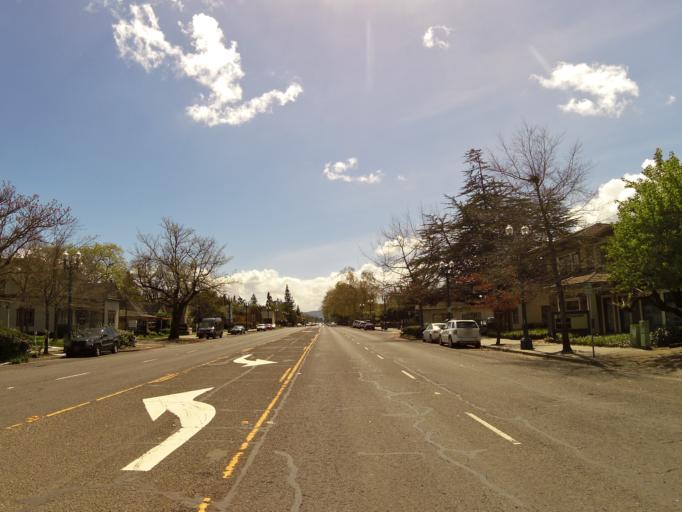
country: US
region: California
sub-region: Sonoma County
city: Sonoma
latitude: 38.2899
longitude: -122.4582
